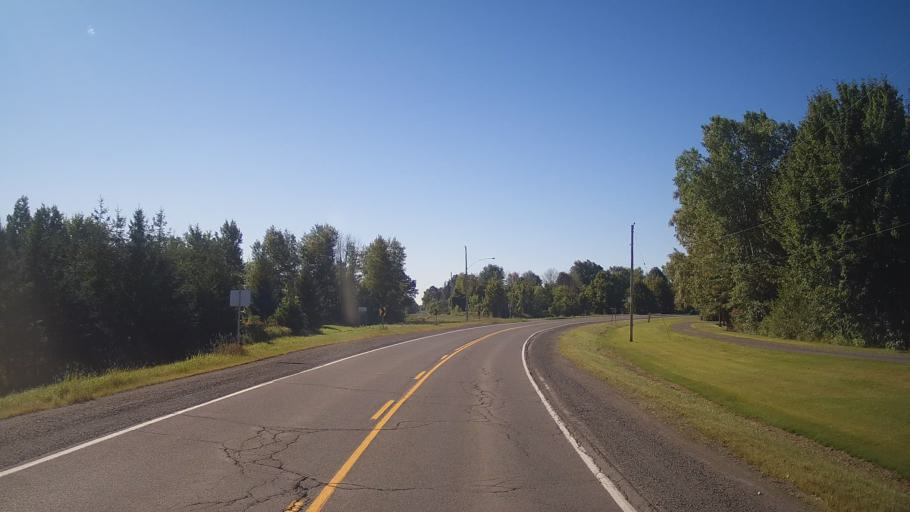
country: CA
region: Ontario
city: Bells Corners
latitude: 45.1066
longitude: -75.6137
